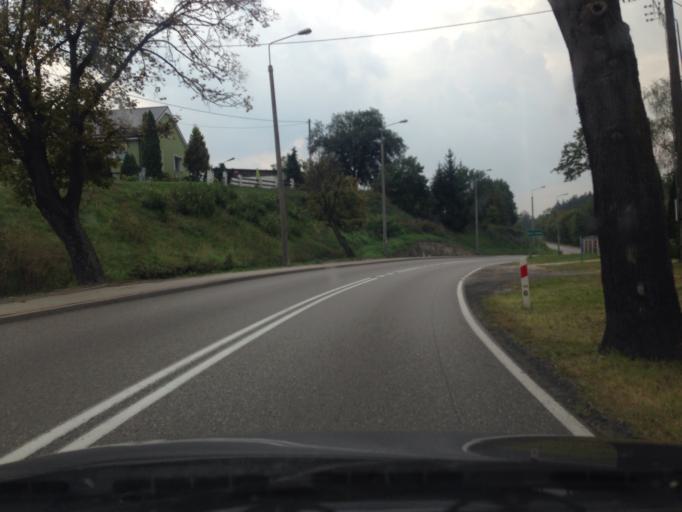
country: PL
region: Pomeranian Voivodeship
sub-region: Powiat kwidzynski
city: Ryjewo
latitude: 53.7991
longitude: 18.9647
